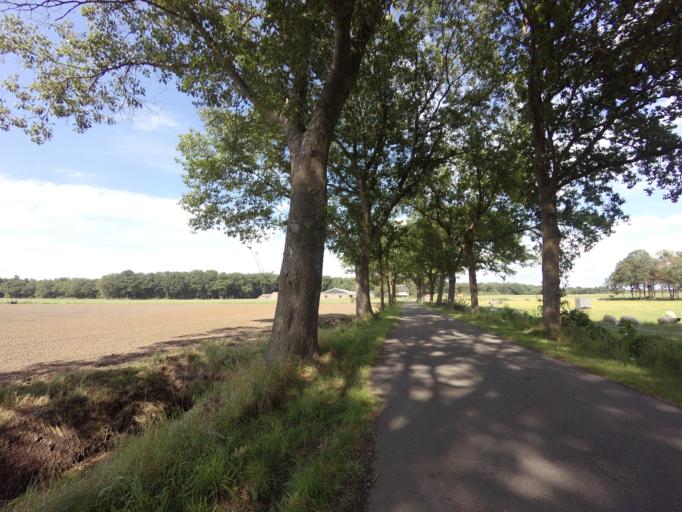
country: NL
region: Overijssel
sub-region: Gemeente Deventer
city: Schalkhaar
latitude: 52.2810
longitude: 6.2414
